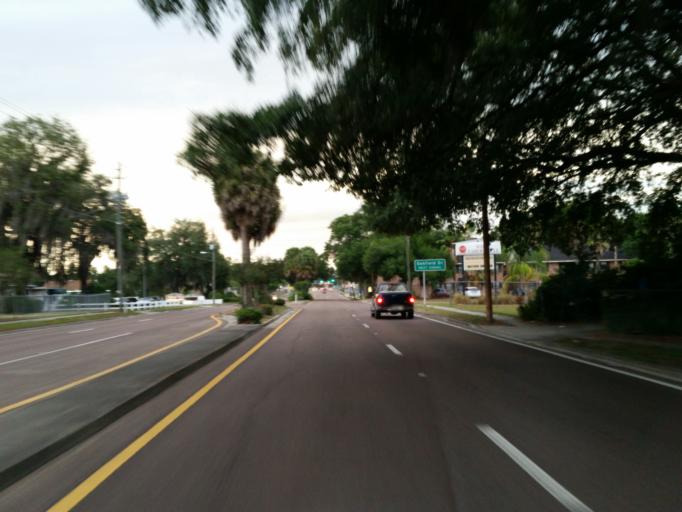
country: US
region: Florida
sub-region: Hillsborough County
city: Brandon
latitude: 27.9312
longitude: -82.2939
